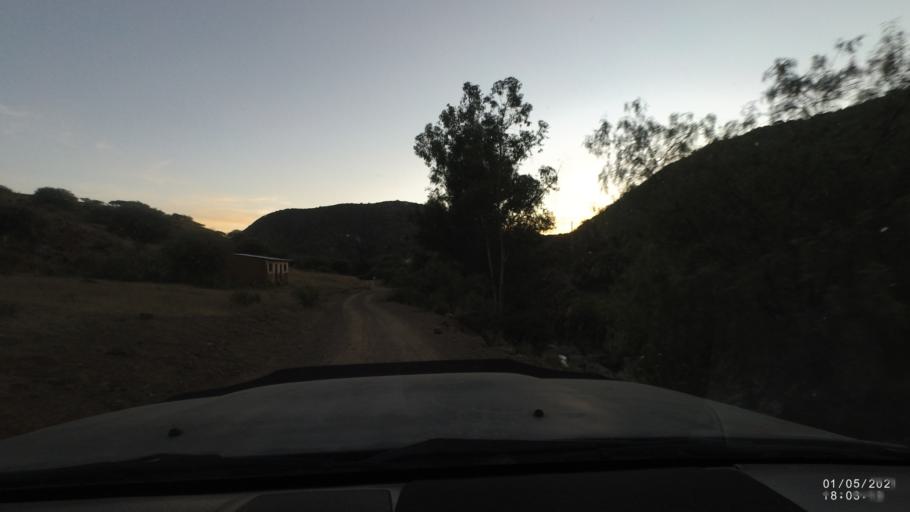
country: BO
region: Cochabamba
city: Capinota
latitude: -17.6886
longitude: -66.1757
